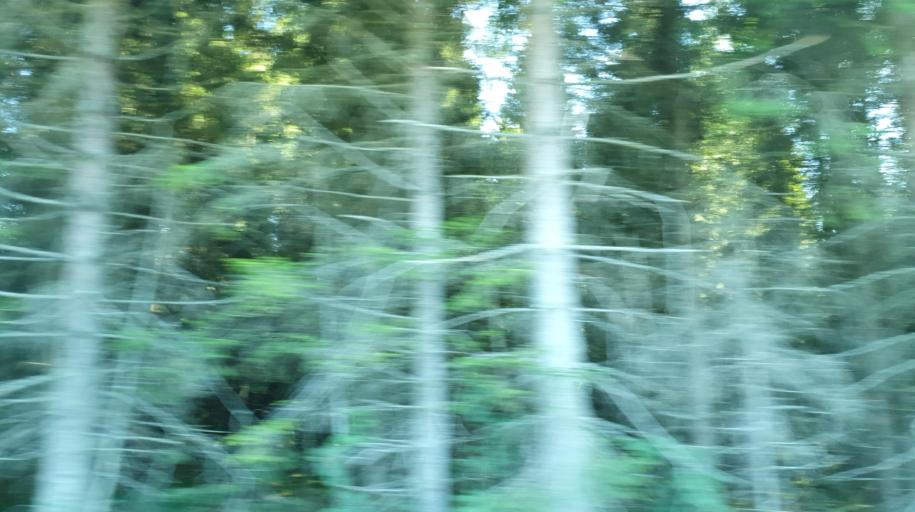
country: NO
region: Nord-Trondelag
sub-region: Levanger
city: Levanger
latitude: 63.6964
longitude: 11.2717
